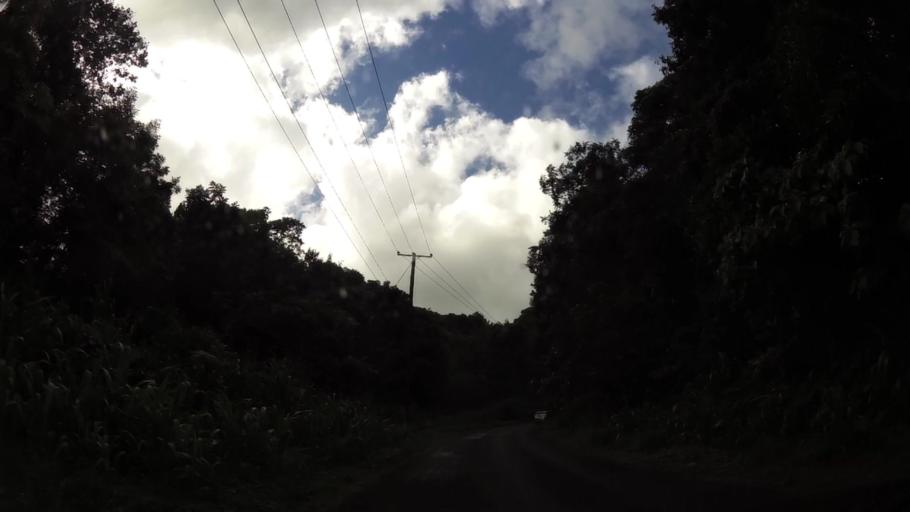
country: DM
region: Saint Paul
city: Pont Casse
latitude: 15.3999
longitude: -61.3089
